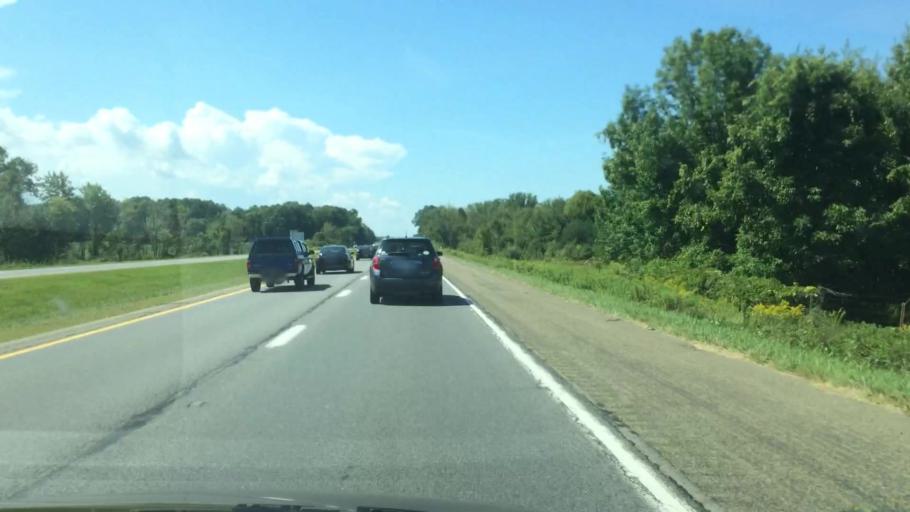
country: US
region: Pennsylvania
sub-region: Erie County
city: Fairview
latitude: 42.0109
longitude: -80.2260
